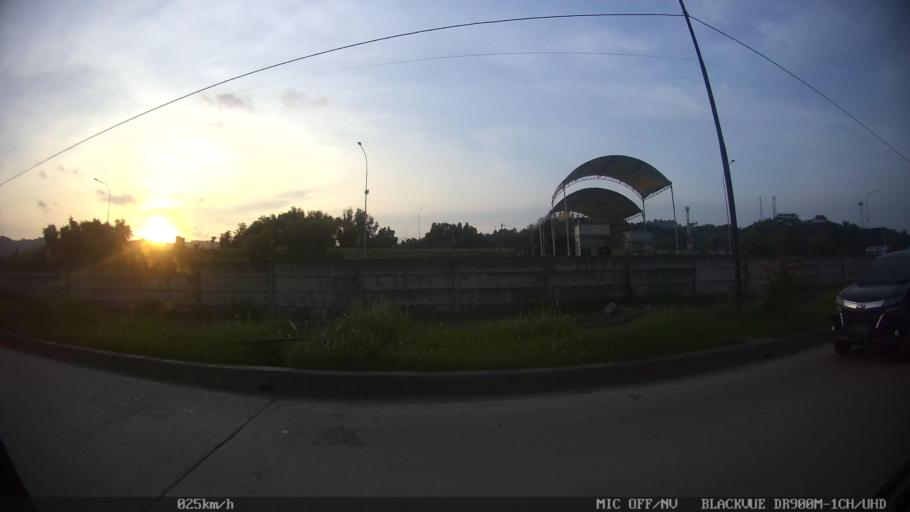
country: ID
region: Lampung
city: Penengahan
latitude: -5.8698
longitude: 105.7526
